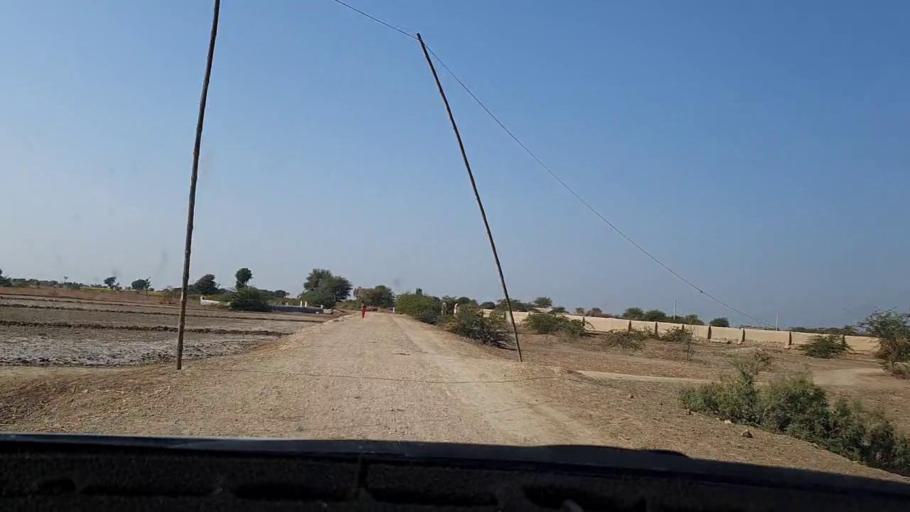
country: PK
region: Sindh
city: Tando Mittha Khan
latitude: 25.8145
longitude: 69.2895
